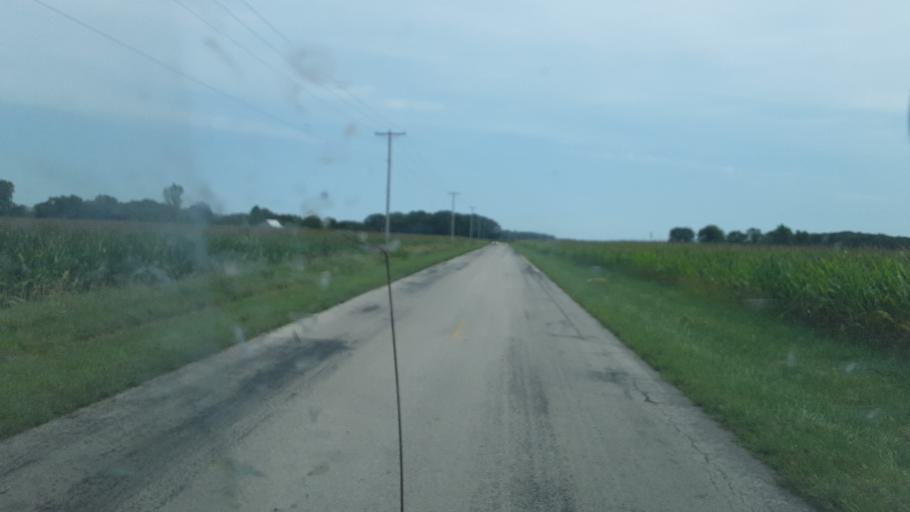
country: US
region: Ohio
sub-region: Union County
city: Richwood
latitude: 40.6003
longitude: -83.3199
